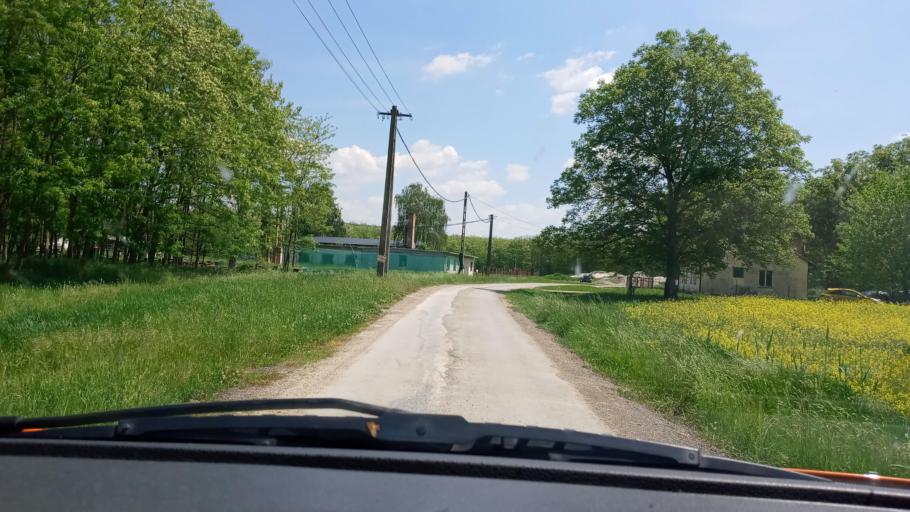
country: HU
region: Baranya
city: Siklos
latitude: 45.7705
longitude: 18.2858
